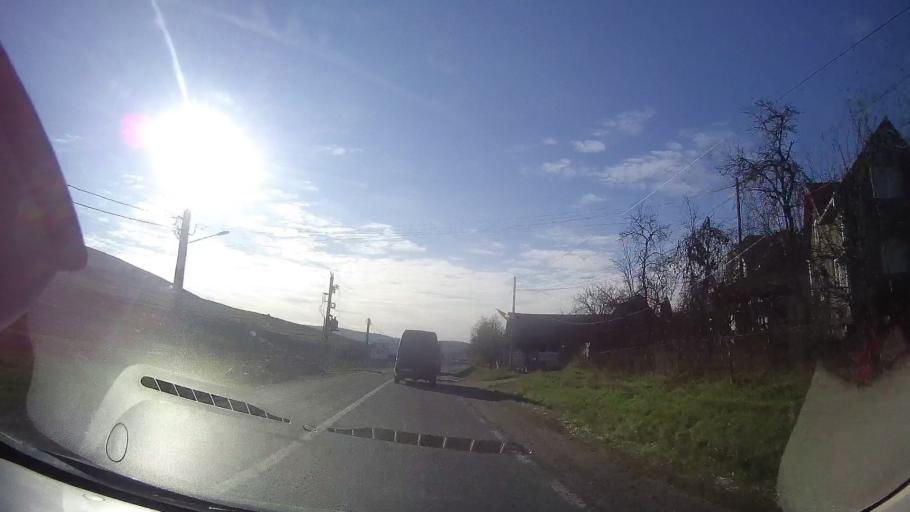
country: RO
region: Cluj
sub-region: Comuna Caianu
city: Vaida-Camaras
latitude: 46.8055
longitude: 23.9632
